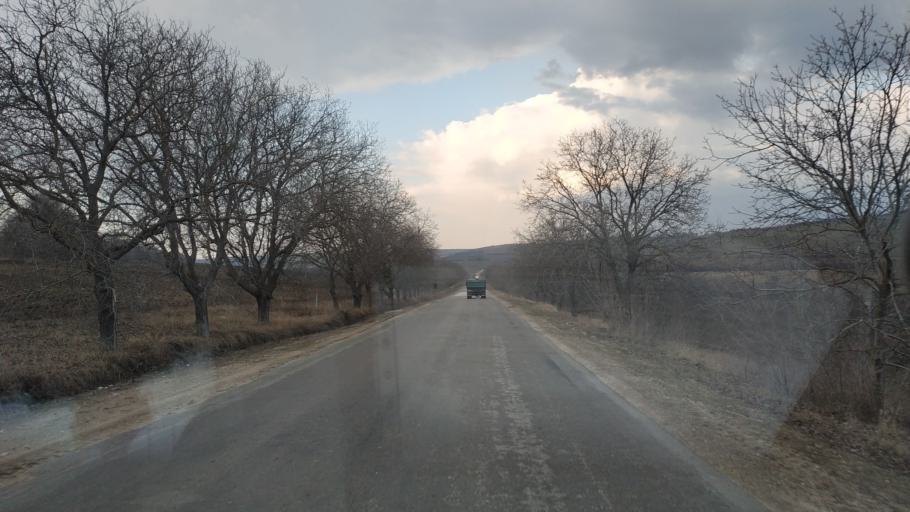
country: MD
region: Anenii Noi
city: Anenii Noi
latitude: 46.9368
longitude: 29.2855
